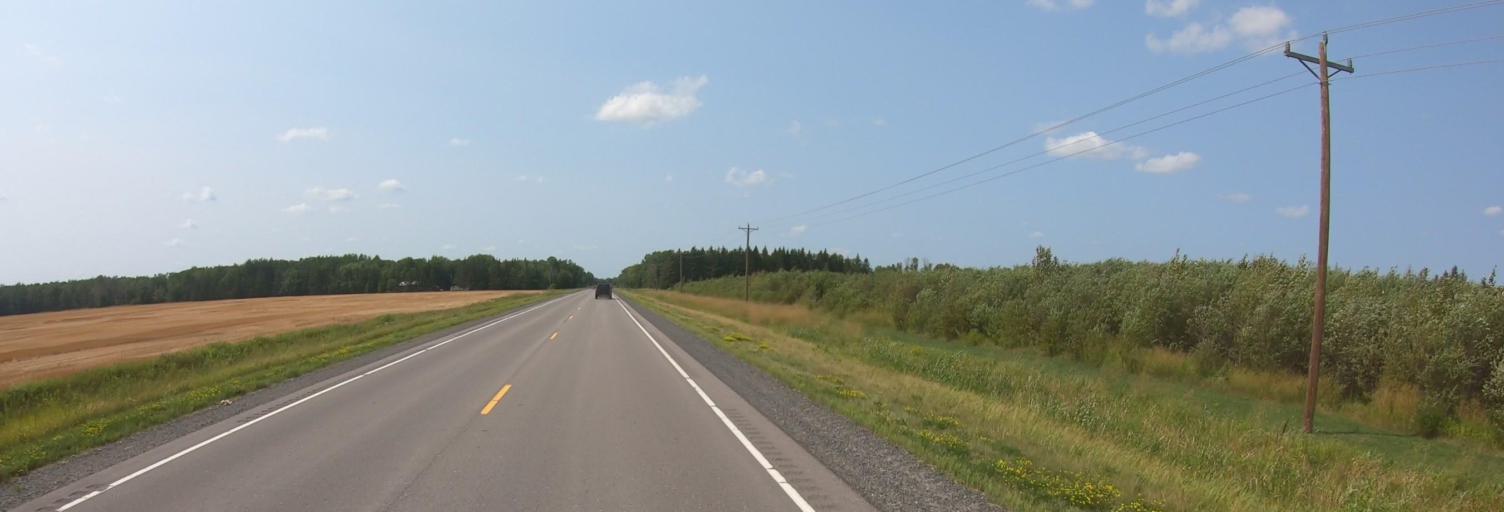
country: US
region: Minnesota
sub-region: Lake of the Woods County
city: Baudette
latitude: 48.6973
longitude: -94.5207
